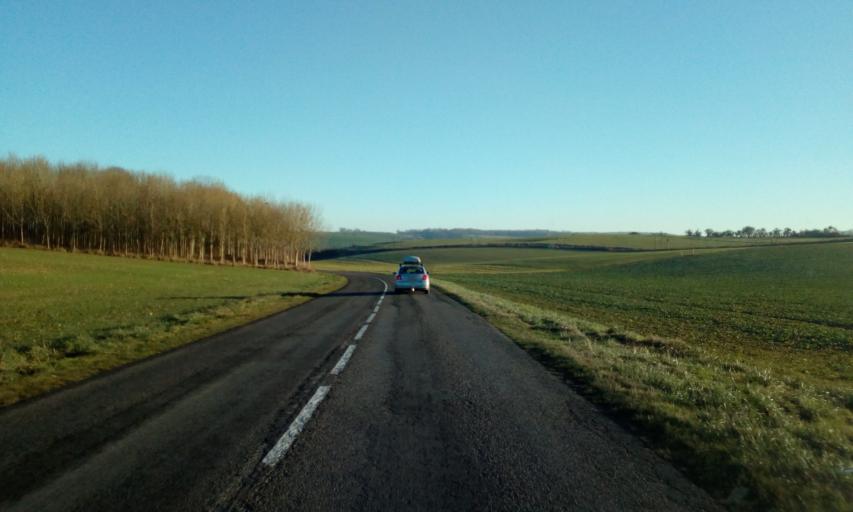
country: FR
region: Champagne-Ardenne
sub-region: Departement des Ardennes
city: Signy-le-Petit
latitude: 49.7797
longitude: 4.3758
